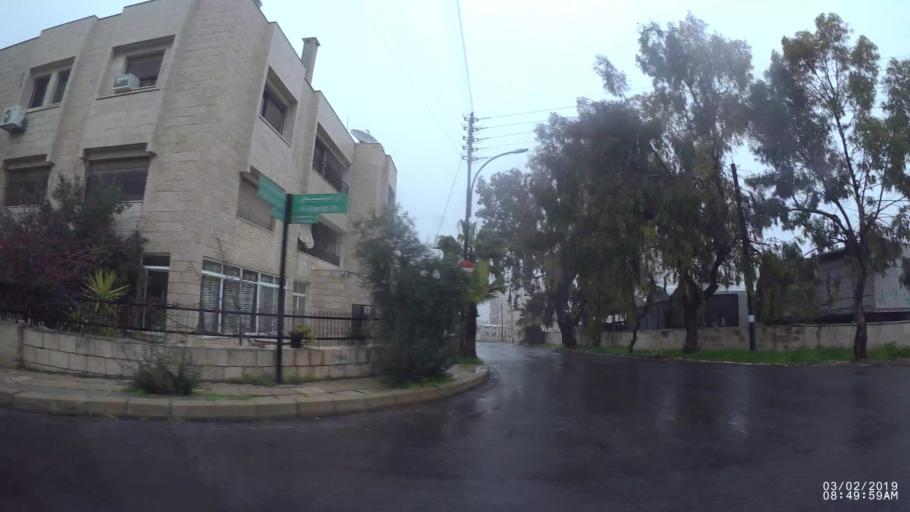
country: JO
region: Amman
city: Wadi as Sir
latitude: 31.9625
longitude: 35.8797
